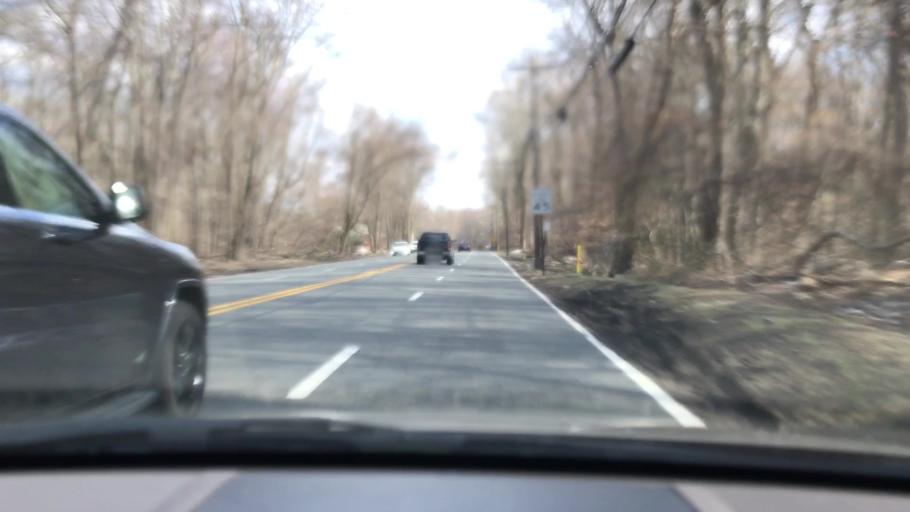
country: US
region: New Jersey
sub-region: Bergen County
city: River Vale
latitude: 40.9808
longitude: -74.0030
